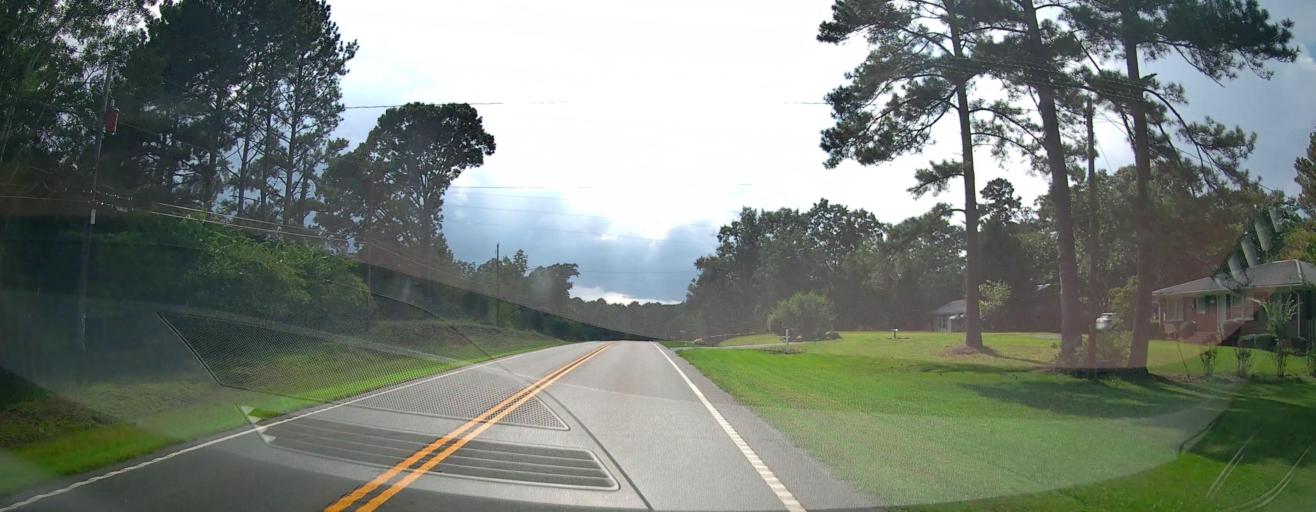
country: US
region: Georgia
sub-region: Meriwether County
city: Manchester
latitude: 32.9873
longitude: -84.5849
